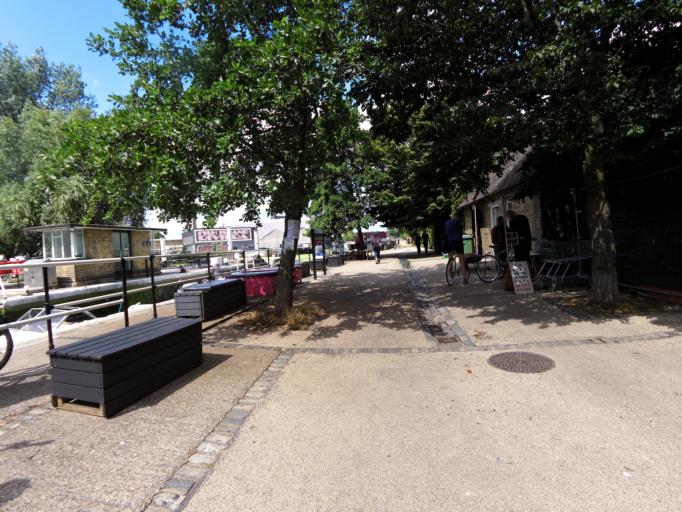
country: GB
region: England
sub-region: Greater London
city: Poplar
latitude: 51.5379
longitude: -0.0208
